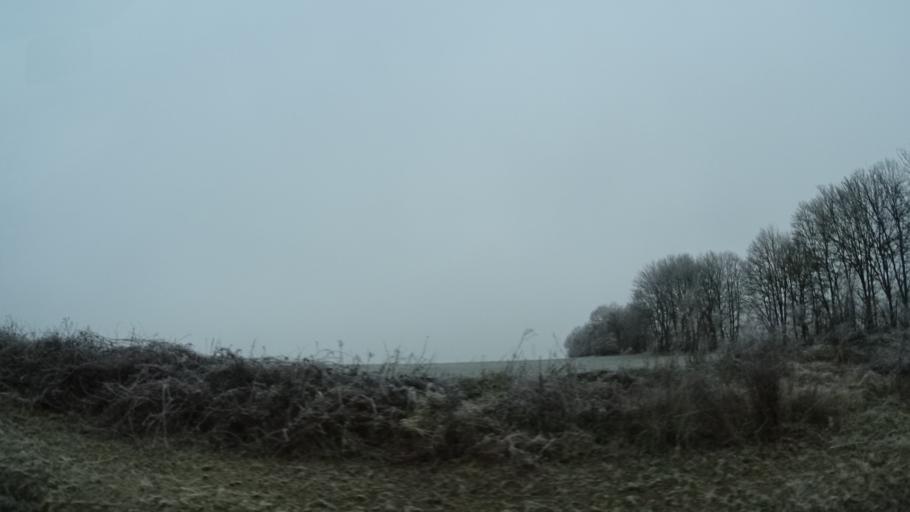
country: DE
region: Bavaria
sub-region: Regierungsbezirk Unterfranken
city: Burgpreppach
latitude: 50.1313
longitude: 10.6277
